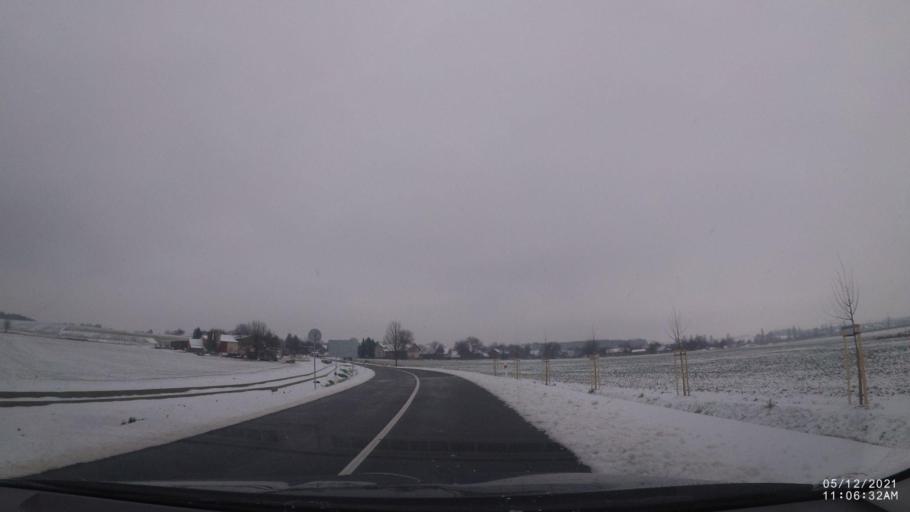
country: CZ
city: Solnice
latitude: 50.1826
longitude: 16.2202
